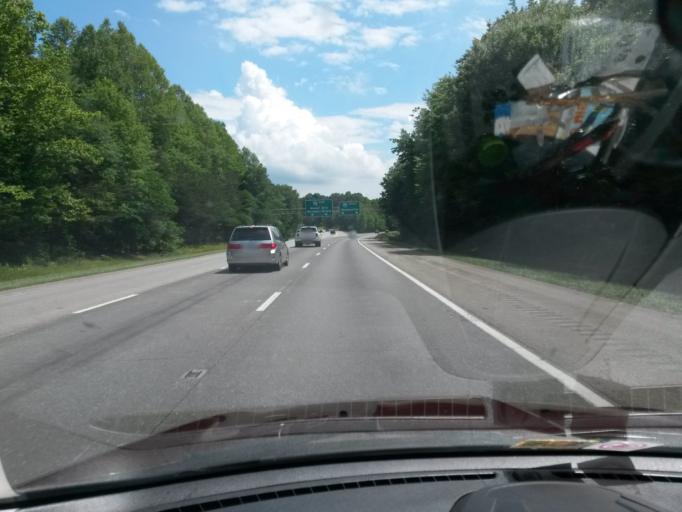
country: US
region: North Carolina
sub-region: Surry County
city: Dobson
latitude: 36.4992
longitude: -80.7425
